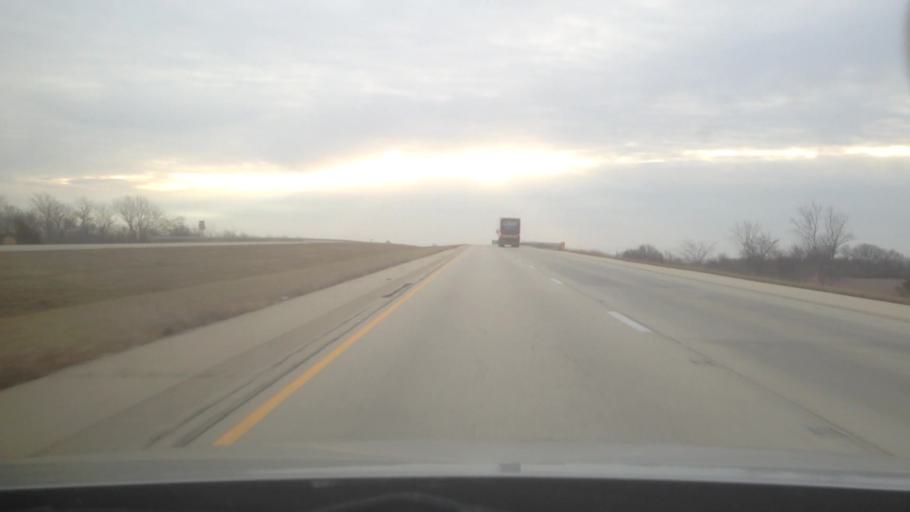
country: US
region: Illinois
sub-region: Macon County
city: Decatur
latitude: 39.8029
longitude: -89.0128
